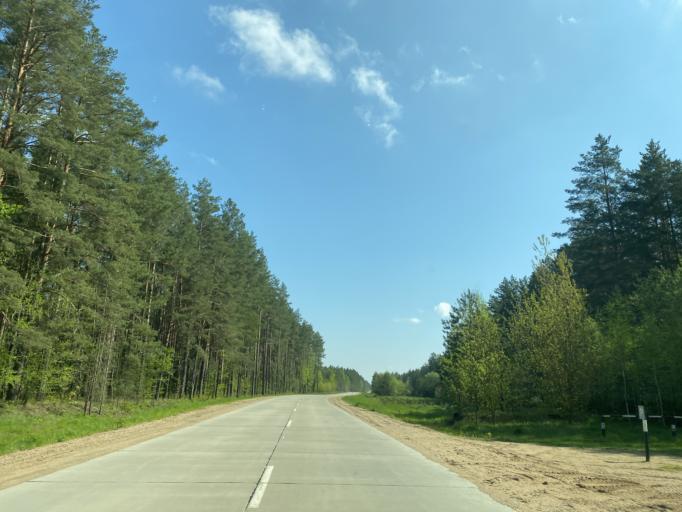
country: BY
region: Minsk
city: Horad Barysaw
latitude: 54.1639
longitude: 28.4996
